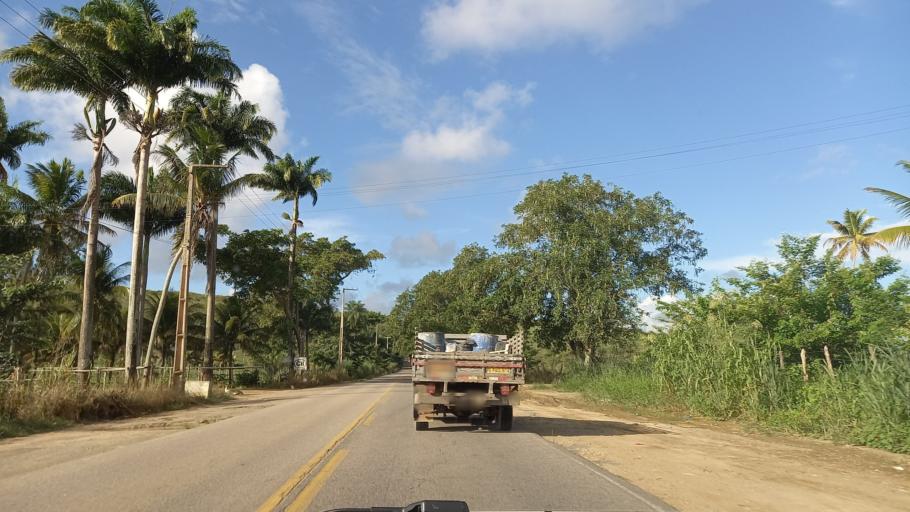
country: BR
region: Pernambuco
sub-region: Rio Formoso
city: Rio Formoso
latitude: -8.6554
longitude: -35.1371
